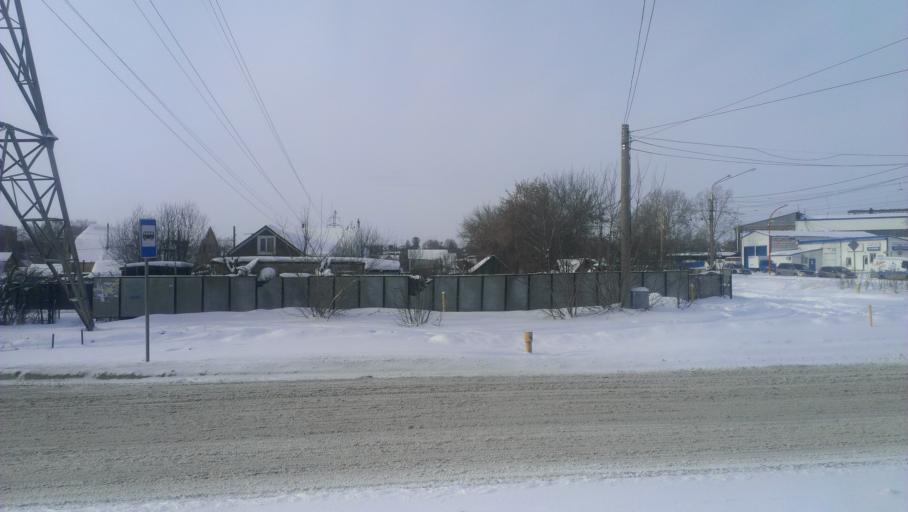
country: RU
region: Altai Krai
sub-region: Gorod Barnaulskiy
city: Barnaul
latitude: 53.3869
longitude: 83.6840
